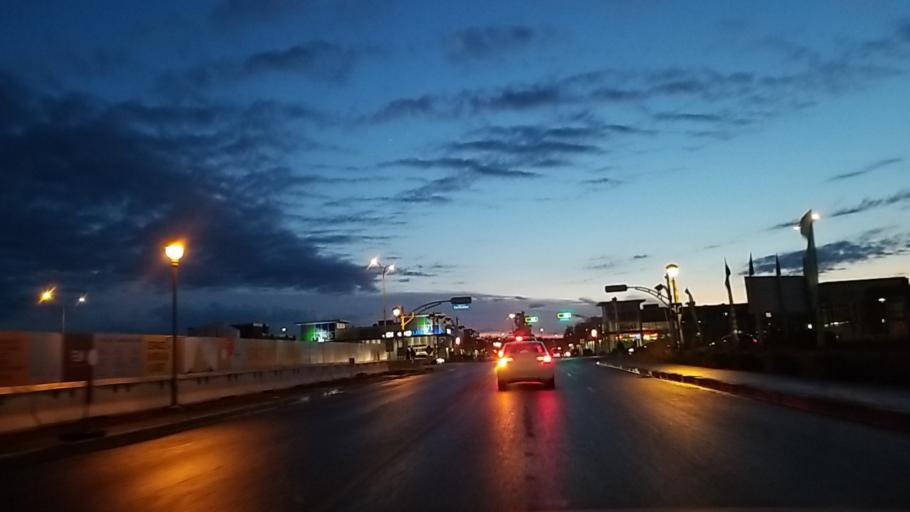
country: CA
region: Quebec
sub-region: Laval
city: Laval
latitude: 45.5578
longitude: -73.7237
